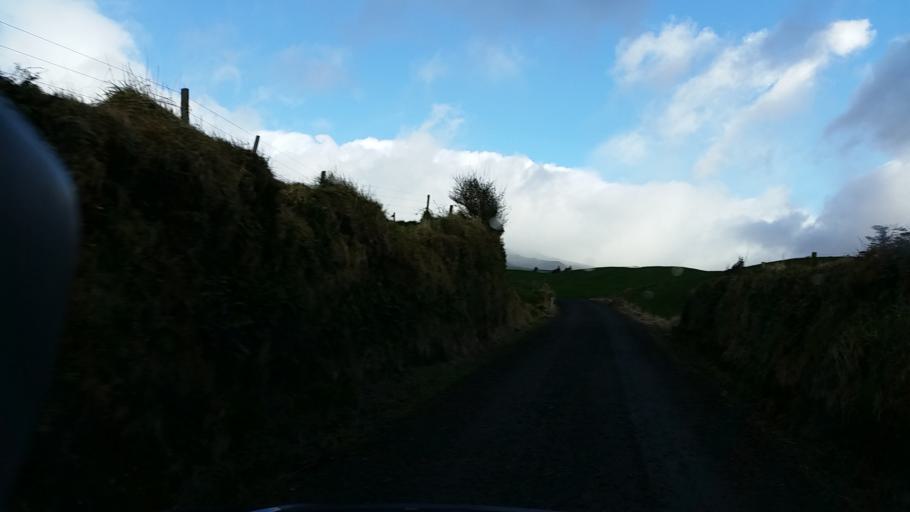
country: NZ
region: Taranaki
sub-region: South Taranaki District
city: Eltham
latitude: -39.3326
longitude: 174.1739
